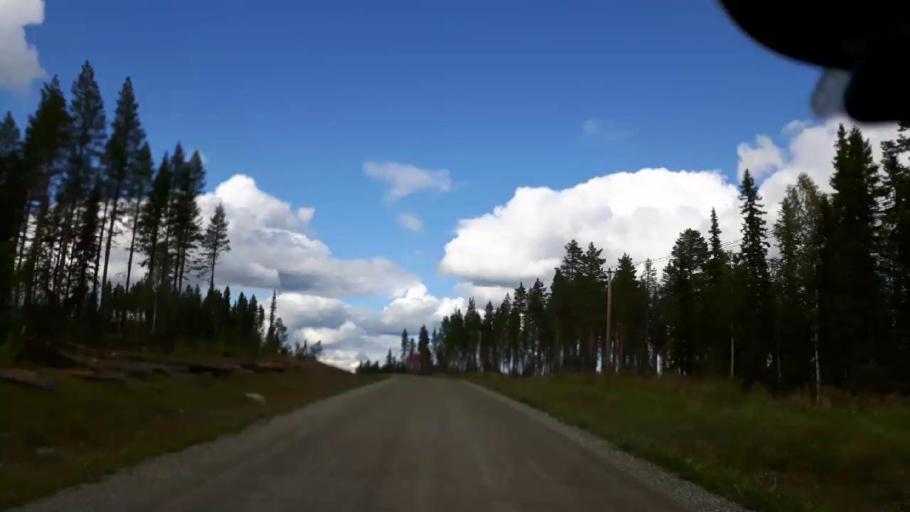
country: SE
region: Jaemtland
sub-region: Stroemsunds Kommun
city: Stroemsund
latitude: 63.3895
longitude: 15.5669
